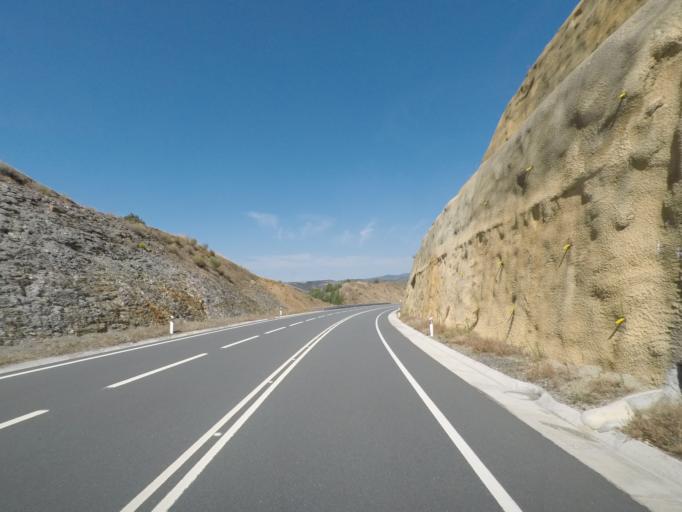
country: PT
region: Braganca
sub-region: Alfandega da Fe
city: Alfandega da Fe
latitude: 41.2969
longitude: -6.8987
